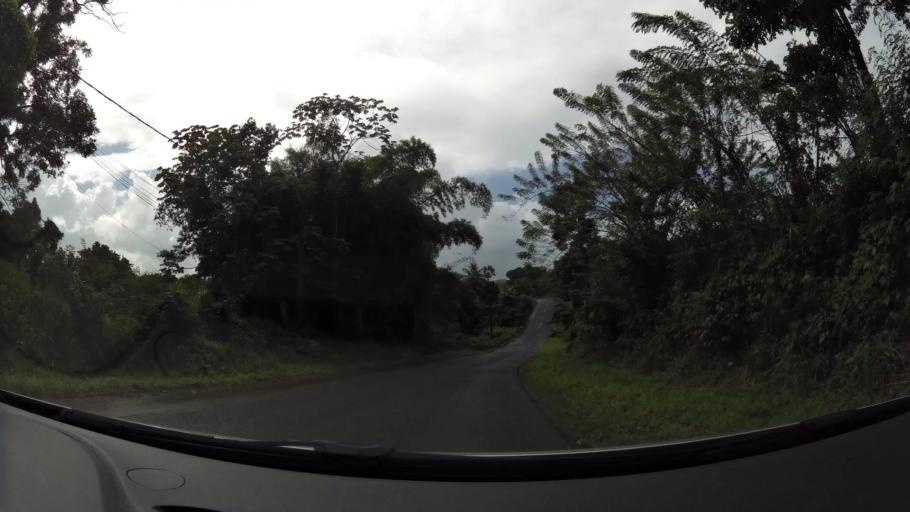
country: MQ
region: Martinique
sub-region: Martinique
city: Saint-Joseph
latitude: 14.6507
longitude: -61.0419
